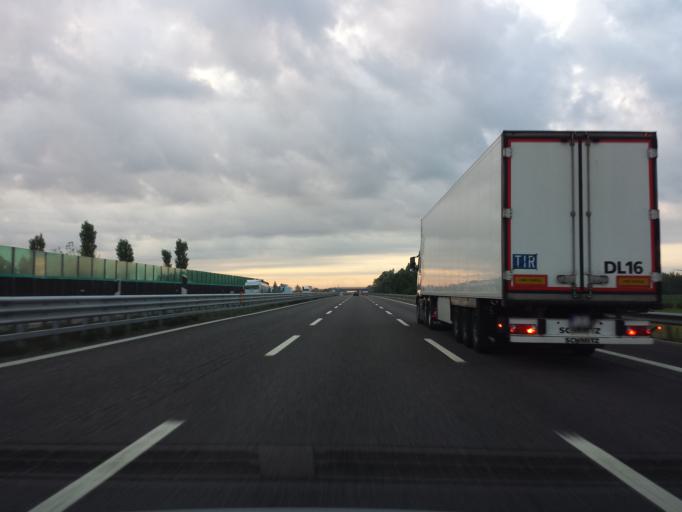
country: IT
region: Veneto
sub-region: Provincia di Padova
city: Ronchi di Campanile
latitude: 45.4632
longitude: 11.7676
